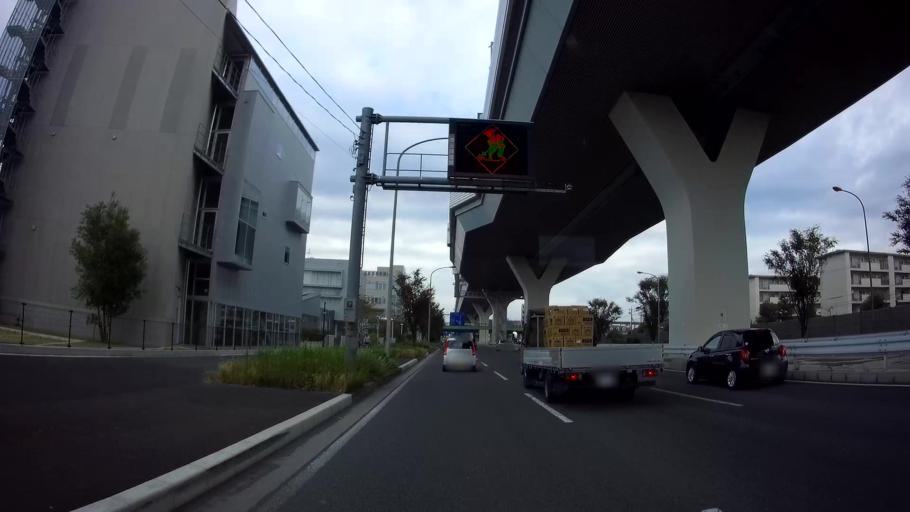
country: JP
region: Saitama
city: Yono
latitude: 35.8414
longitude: 139.6277
